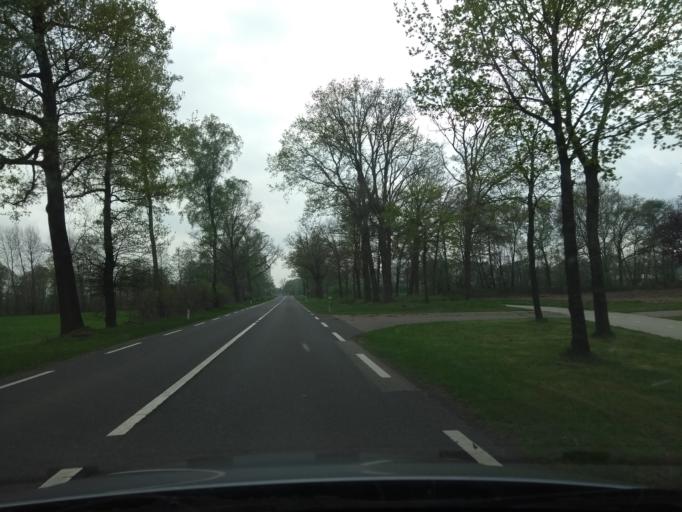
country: NL
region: Overijssel
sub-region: Gemeente Oldenzaal
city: Oldenzaal
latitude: 52.3821
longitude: 6.9001
